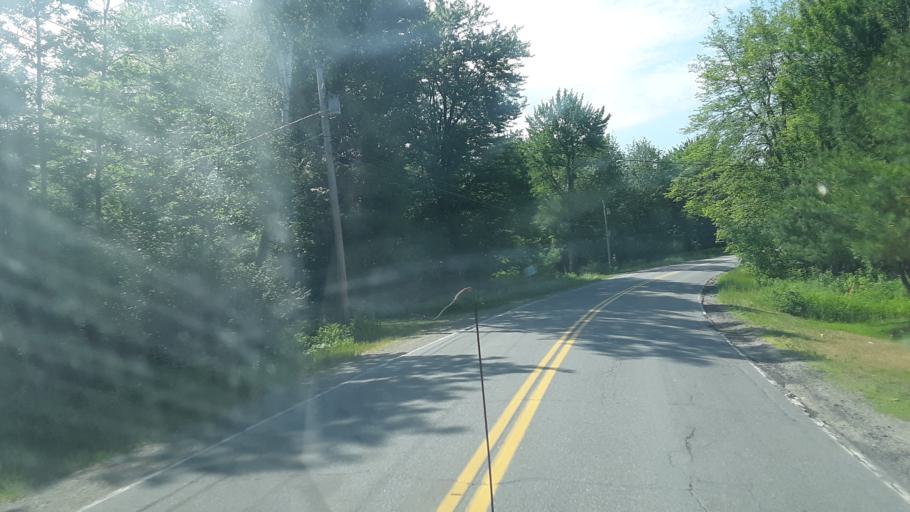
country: US
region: Maine
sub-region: Waldo County
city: Swanville
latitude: 44.5582
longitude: -68.9534
